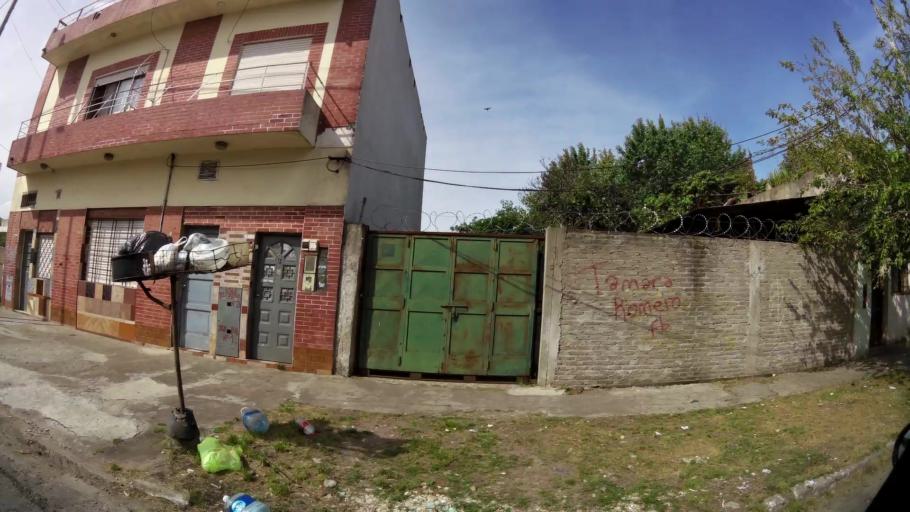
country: AR
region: Buenos Aires
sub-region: Partido de Quilmes
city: Quilmes
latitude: -34.7751
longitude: -58.2357
